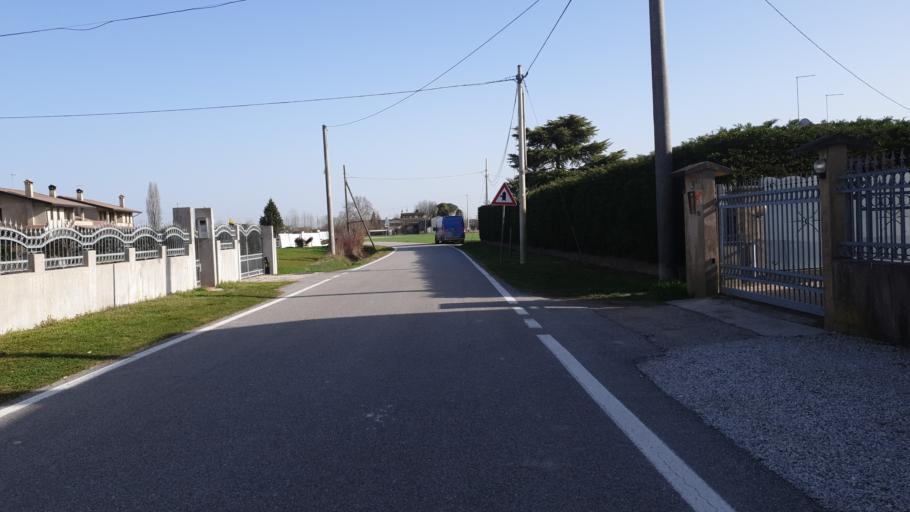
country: IT
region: Veneto
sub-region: Provincia di Padova
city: Vigodarzere
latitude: 45.4750
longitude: 11.8880
